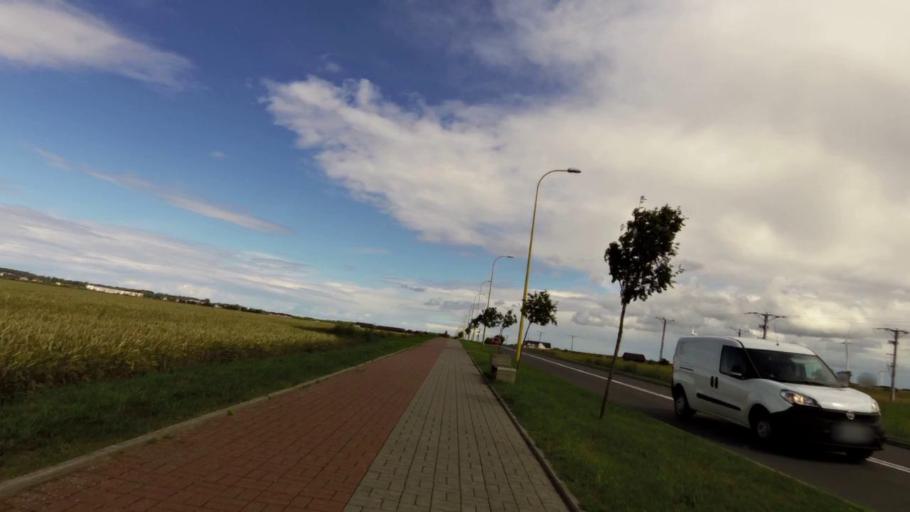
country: PL
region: West Pomeranian Voivodeship
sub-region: Powiat slawienski
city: Darlowo
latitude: 54.4333
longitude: 16.4116
